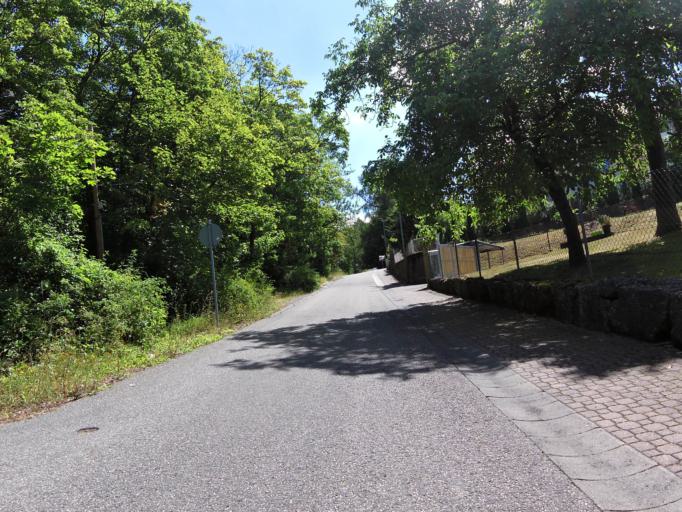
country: DE
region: Bavaria
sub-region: Regierungsbezirk Unterfranken
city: Hochberg
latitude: 49.7847
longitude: 9.9018
